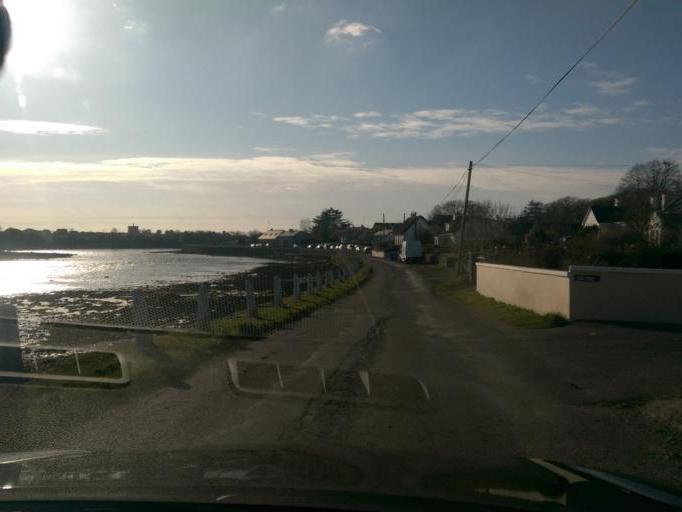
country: IE
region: Connaught
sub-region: County Galway
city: Oranmore
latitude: 53.2110
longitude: -8.8915
